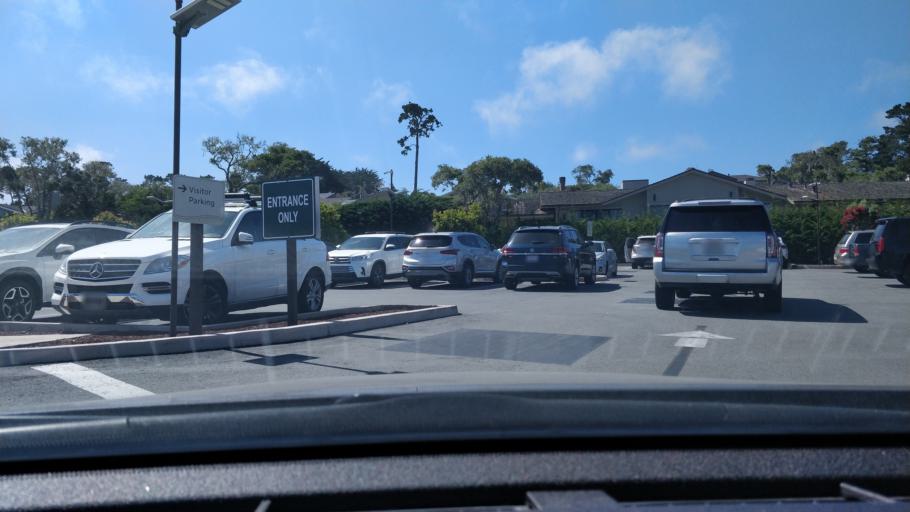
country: US
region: California
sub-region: Monterey County
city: Del Monte Forest
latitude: 36.5697
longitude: -121.9503
